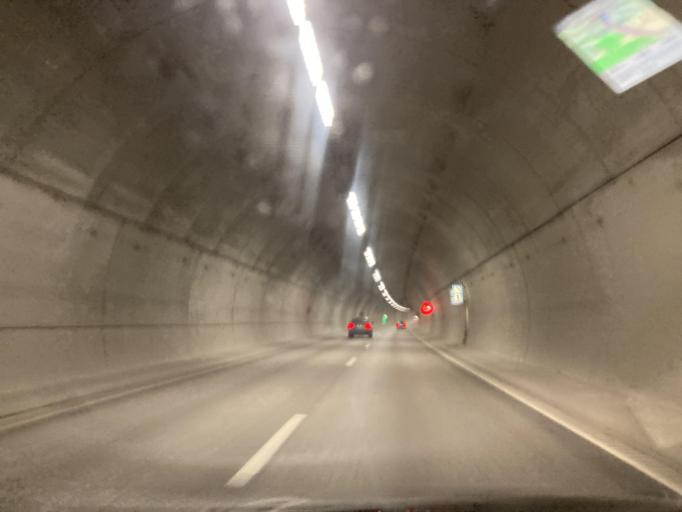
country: NO
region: Akershus
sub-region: Eidsvoll
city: Eidsvoll
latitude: 60.4794
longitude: 11.2432
